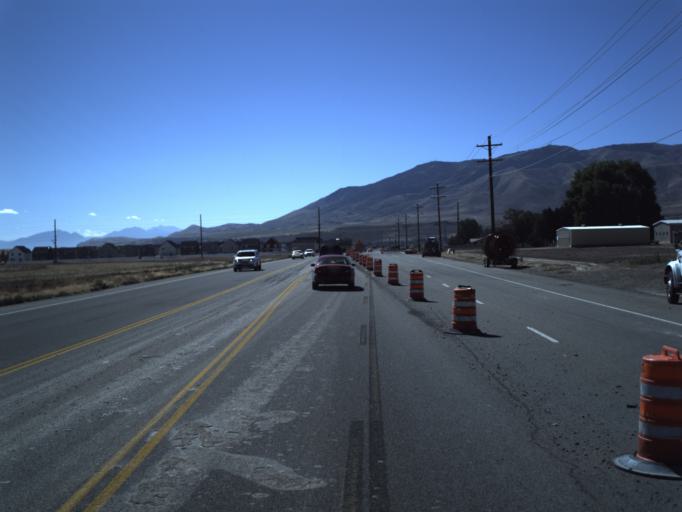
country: US
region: Utah
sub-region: Utah County
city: Saratoga Springs
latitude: 40.3594
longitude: -111.9163
